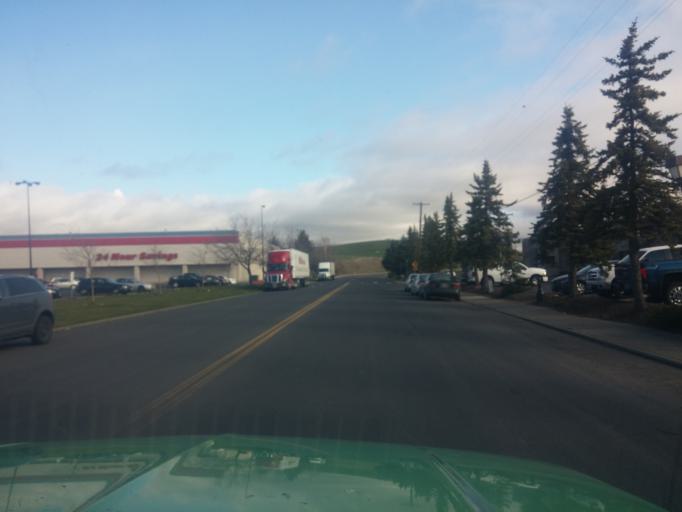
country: US
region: Idaho
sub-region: Latah County
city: Moscow
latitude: 46.7333
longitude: -117.0246
